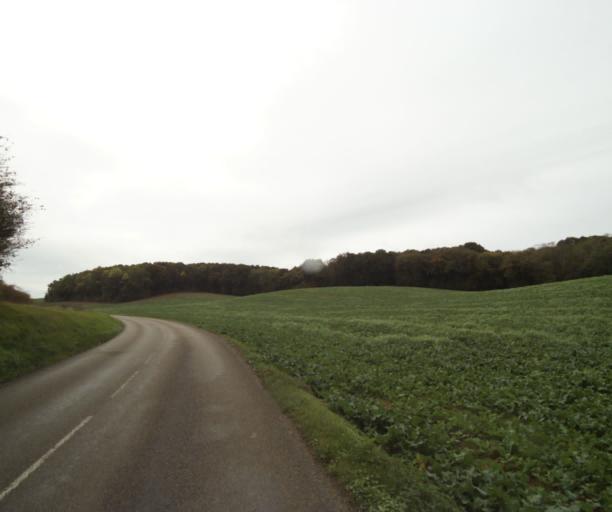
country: FR
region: Centre
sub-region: Departement d'Eure-et-Loir
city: Dreux
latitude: 48.7673
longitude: 1.3515
